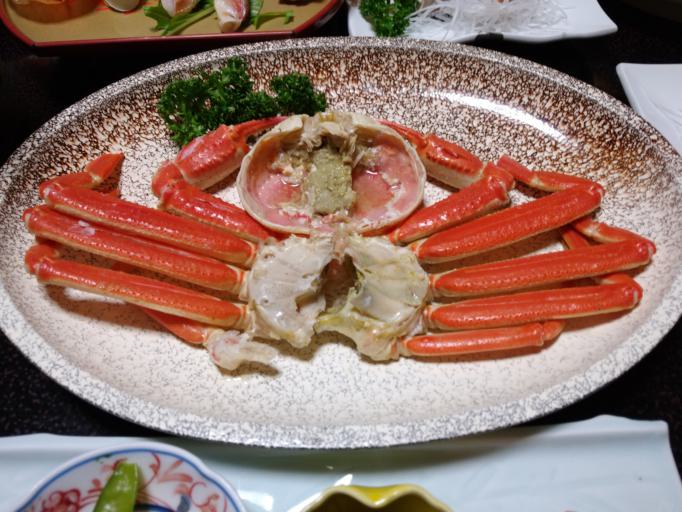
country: JP
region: Hyogo
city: Toyooka
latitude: 35.6289
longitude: 134.8163
